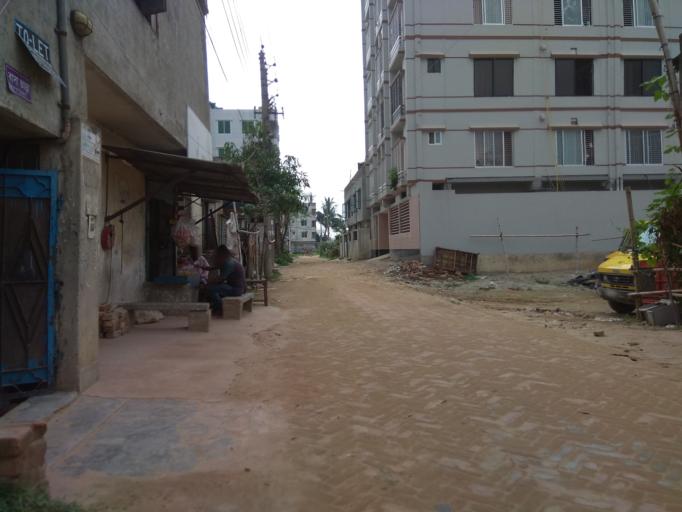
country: BD
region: Dhaka
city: Tungi
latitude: 23.8304
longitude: 90.3523
